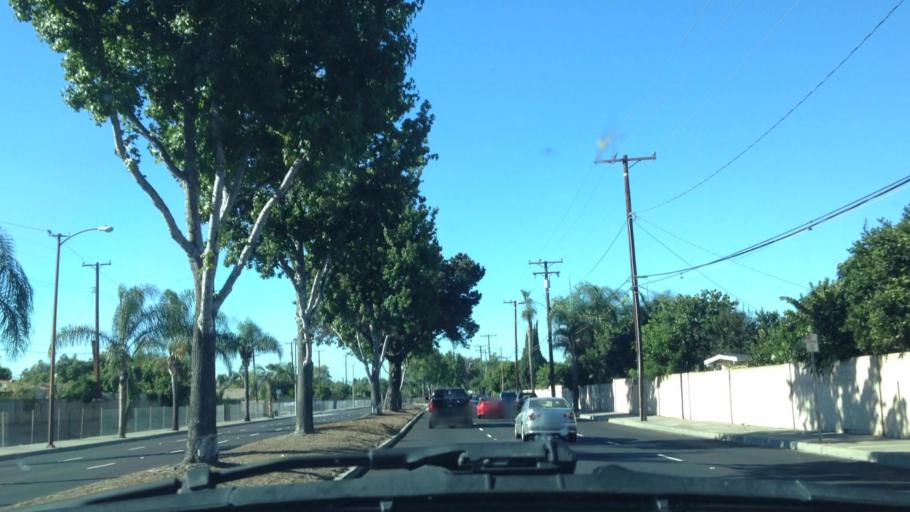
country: US
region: California
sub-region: Orange County
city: Santa Ana
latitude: 33.7302
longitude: -117.9060
